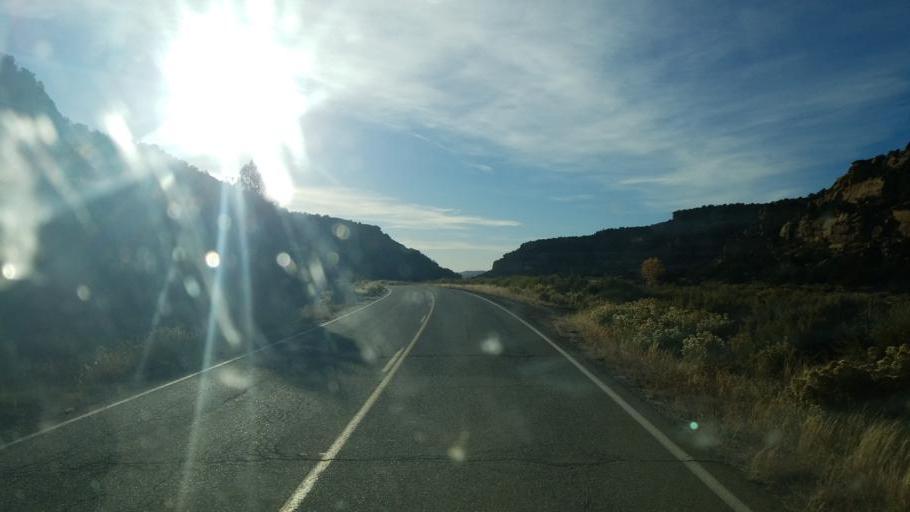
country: US
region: New Mexico
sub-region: San Juan County
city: Bloomfield
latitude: 36.7402
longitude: -107.7240
